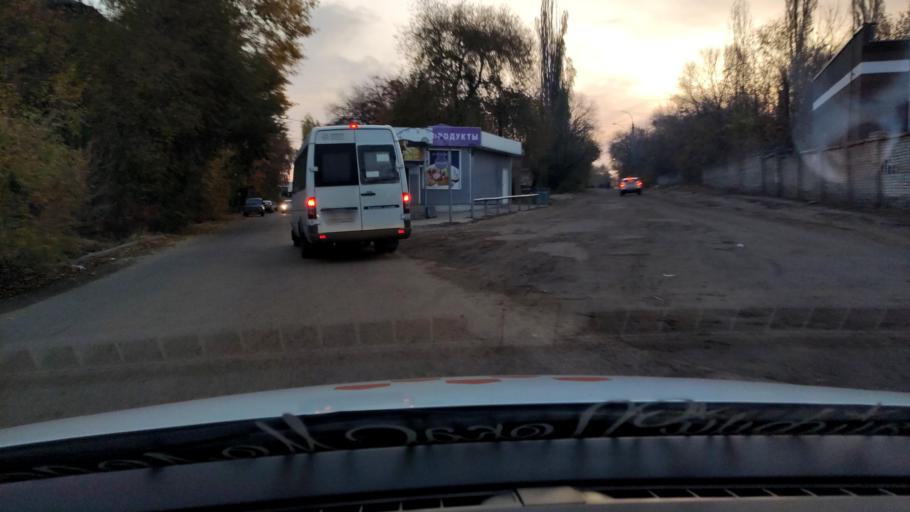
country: RU
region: Voronezj
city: Voronezh
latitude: 51.6915
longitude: 39.1655
